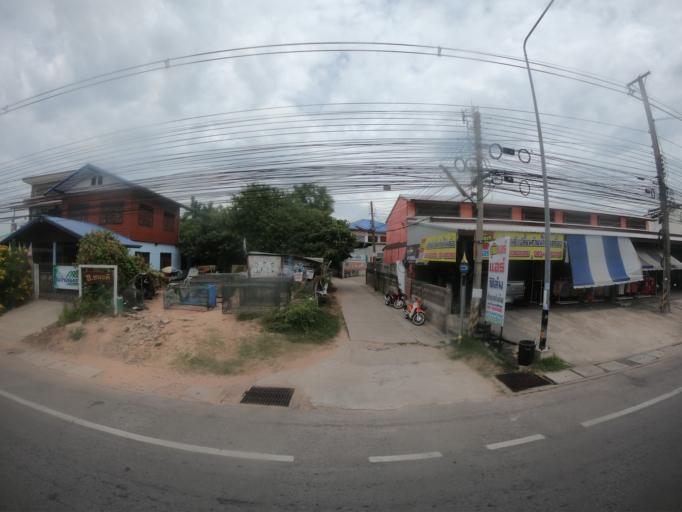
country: TH
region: Maha Sarakham
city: Maha Sarakham
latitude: 16.1746
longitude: 103.3166
